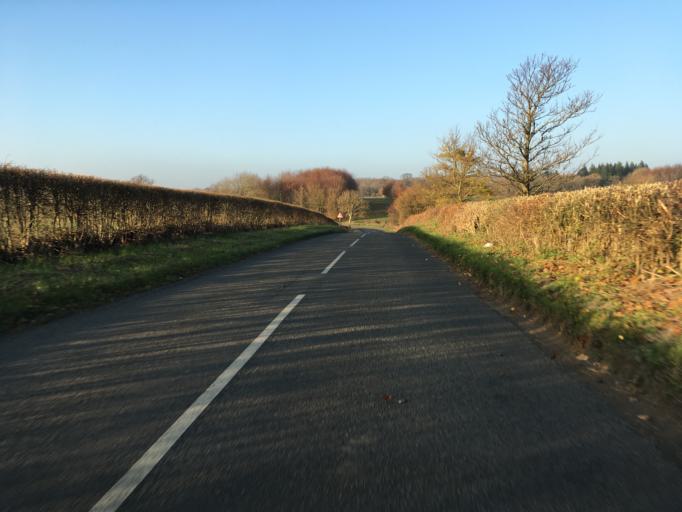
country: GB
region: England
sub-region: Wiltshire
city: Luckington
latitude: 51.5627
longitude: -2.2879
